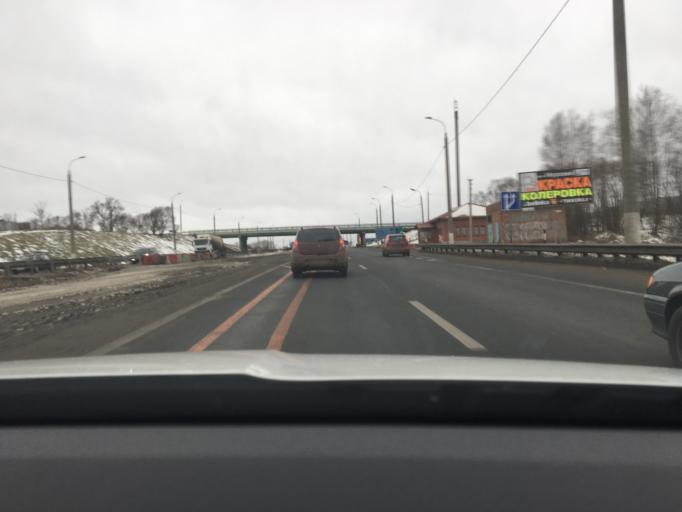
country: RU
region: Moskovskaya
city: Serpukhov
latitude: 54.8567
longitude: 37.4796
